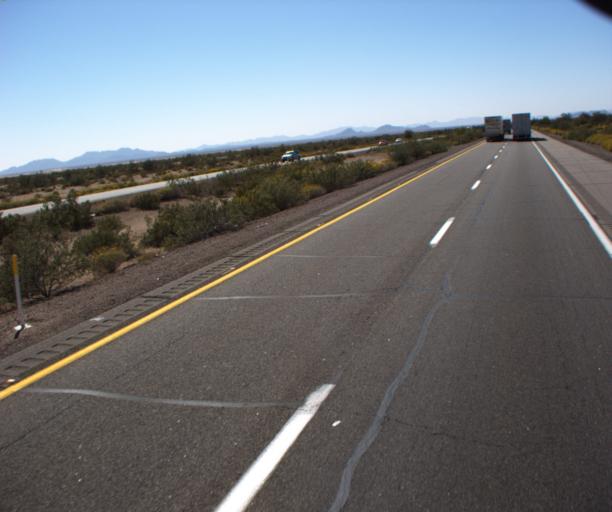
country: US
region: Arizona
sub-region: Yuma County
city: Wellton
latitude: 32.7217
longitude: -113.7689
